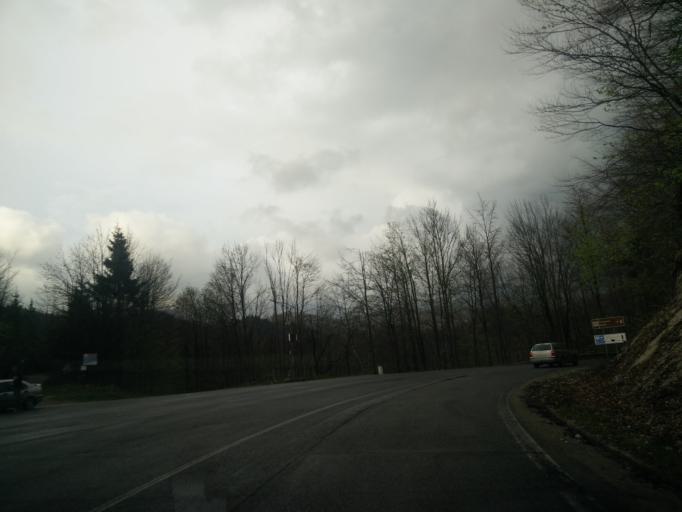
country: SK
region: Banskobystricky
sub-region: Okres Ziar nad Hronom
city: Kremnica
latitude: 48.8384
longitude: 18.9985
